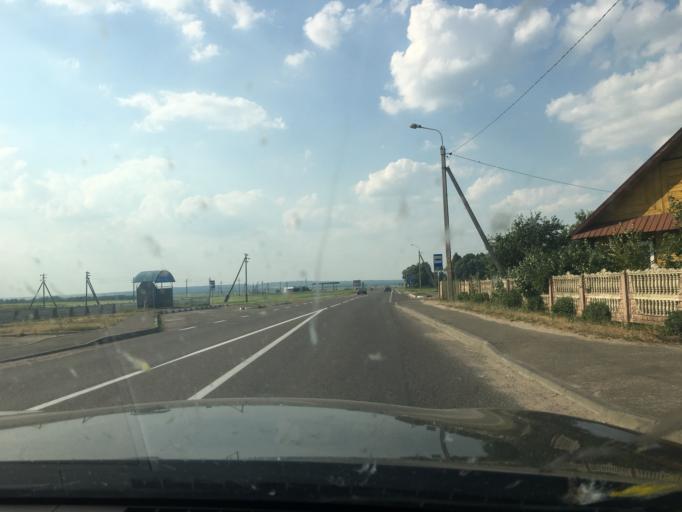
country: BY
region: Grodnenskaya
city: Indura
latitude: 53.3418
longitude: 23.9484
